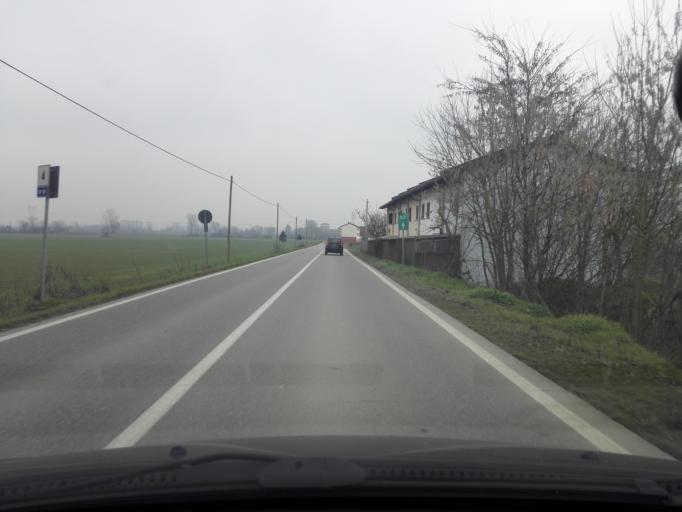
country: IT
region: Piedmont
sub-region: Provincia di Alessandria
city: Casal Cermelli
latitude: 44.8323
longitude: 8.6340
